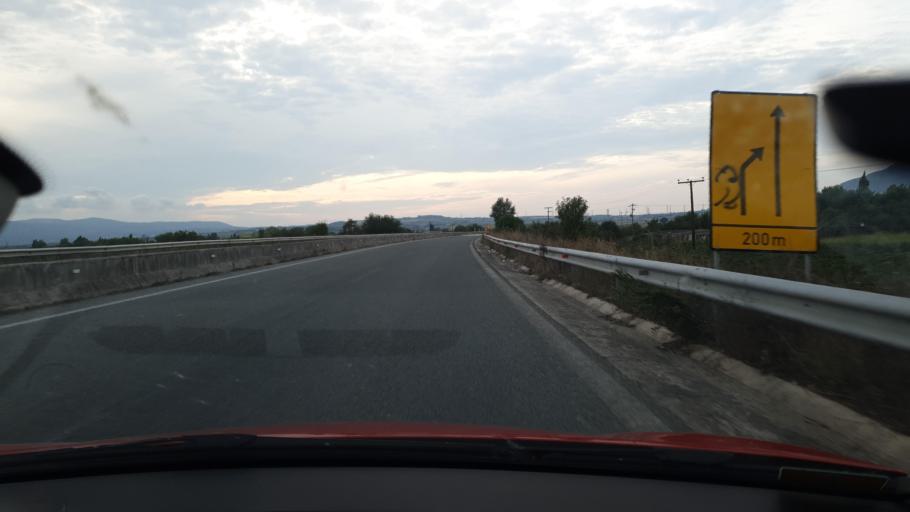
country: GR
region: Central Macedonia
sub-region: Nomos Thessalonikis
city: Assiros
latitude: 40.7836
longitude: 23.0160
